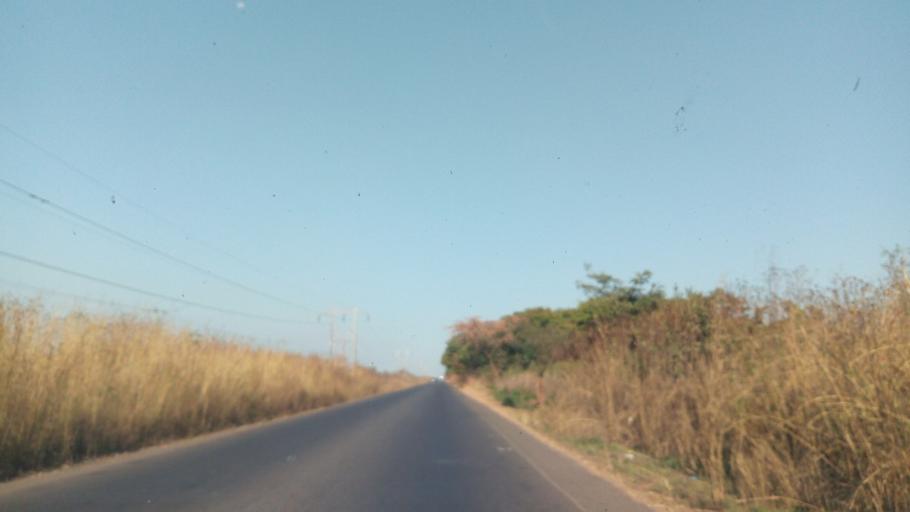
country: CD
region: Katanga
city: Likasi
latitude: -11.0040
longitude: 26.9000
